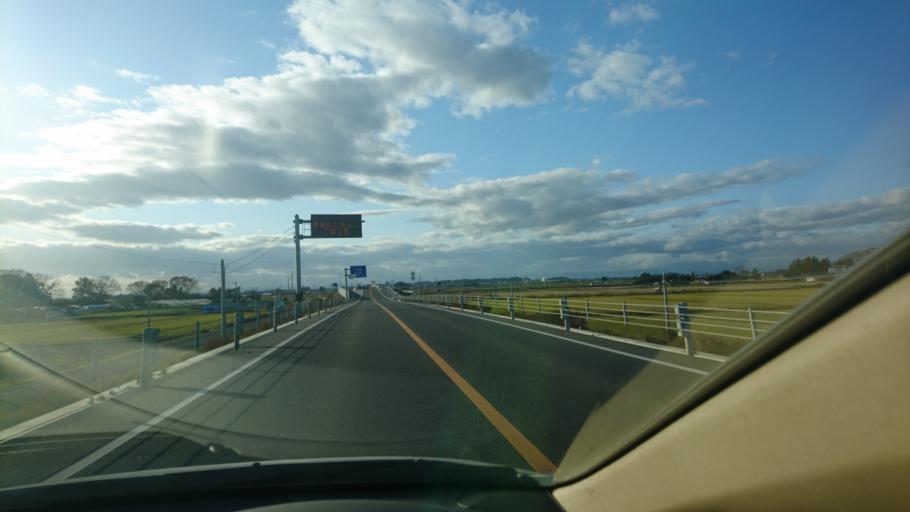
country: JP
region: Miyagi
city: Wakuya
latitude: 38.6856
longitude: 141.2380
